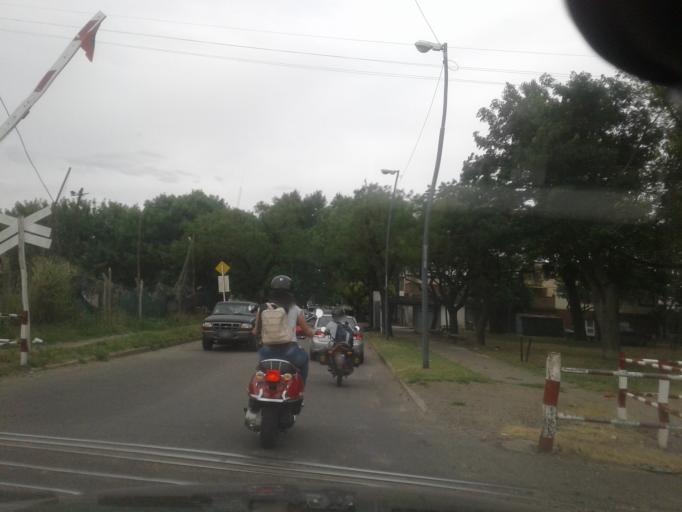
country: AR
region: Santa Fe
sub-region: Departamento de Rosario
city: Rosario
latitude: -32.9315
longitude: -60.6873
